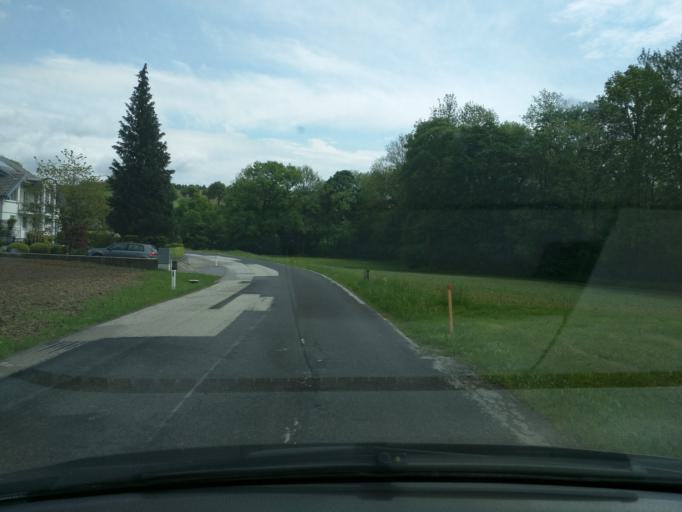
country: AT
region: Lower Austria
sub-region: Politischer Bezirk Amstetten
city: Ferschnitz
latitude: 48.1117
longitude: 15.0064
